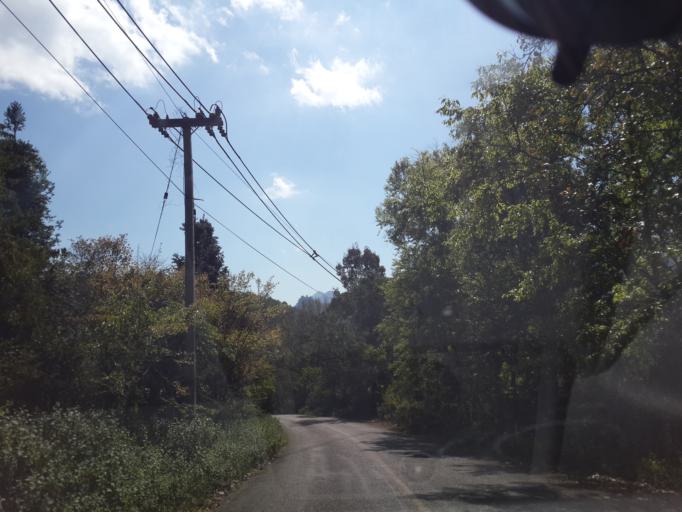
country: TH
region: Chiang Mai
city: Fang
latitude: 19.8988
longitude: 99.0458
